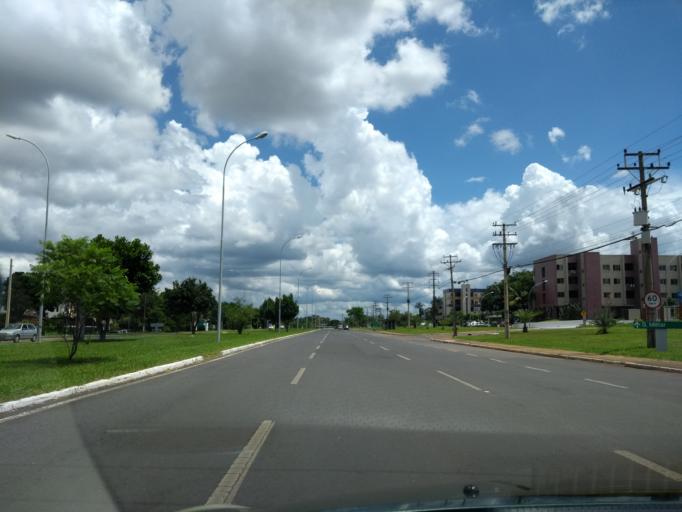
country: BR
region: Federal District
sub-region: Brasilia
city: Brasilia
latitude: -15.7849
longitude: -47.9307
